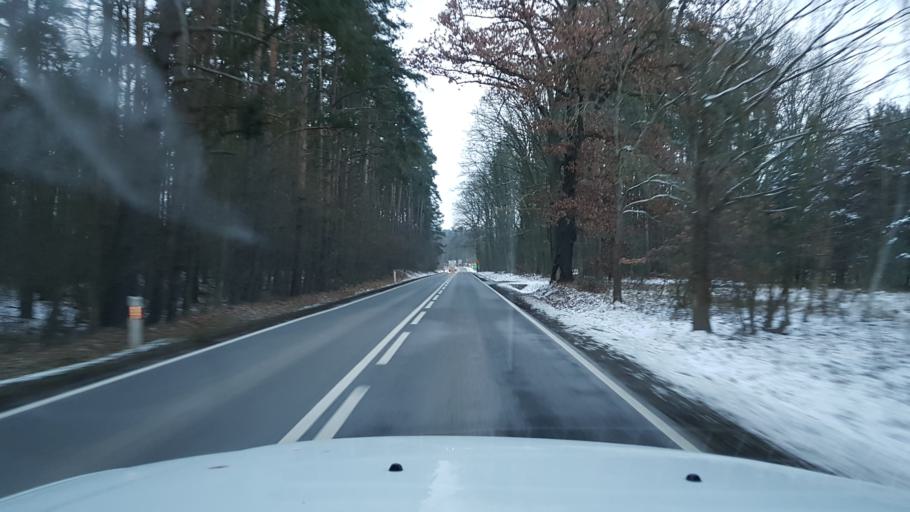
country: PL
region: West Pomeranian Voivodeship
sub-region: Powiat gryfinski
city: Chojna
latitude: 53.0369
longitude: 14.4511
